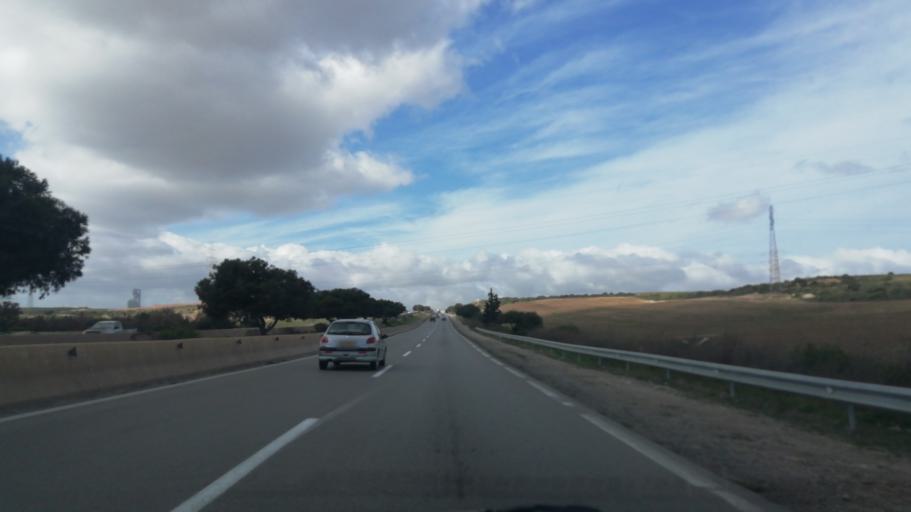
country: DZ
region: Oran
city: Ain el Bya
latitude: 35.7700
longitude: -0.2376
